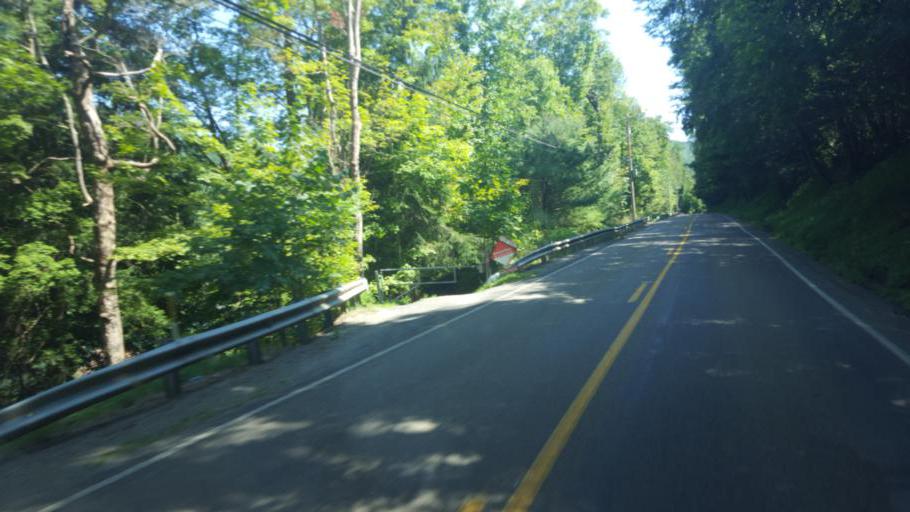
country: US
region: Pennsylvania
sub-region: Clarion County
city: Knox
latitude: 41.1653
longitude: -79.6856
